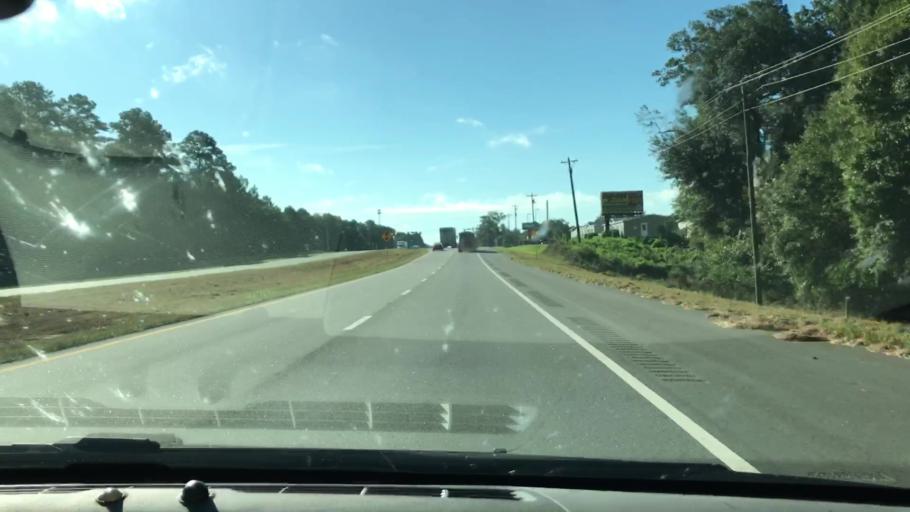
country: US
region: Georgia
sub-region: Lee County
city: Leesburg
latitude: 31.6658
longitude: -84.2824
